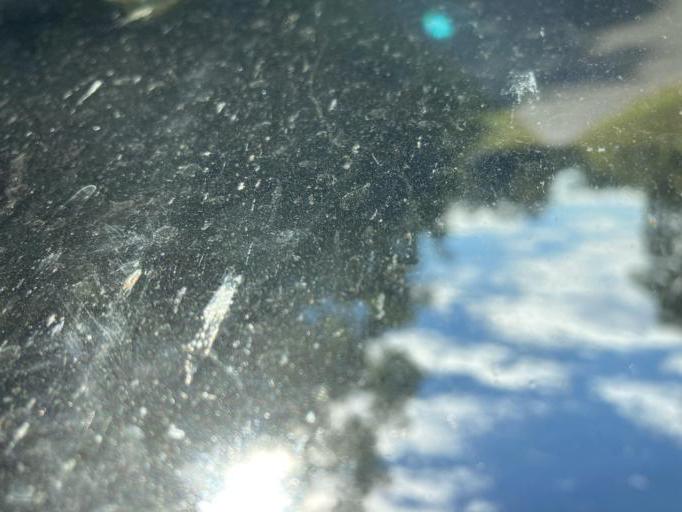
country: US
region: Mississippi
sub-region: Jackson County
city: Saint Martin
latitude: 30.4370
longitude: -88.8687
